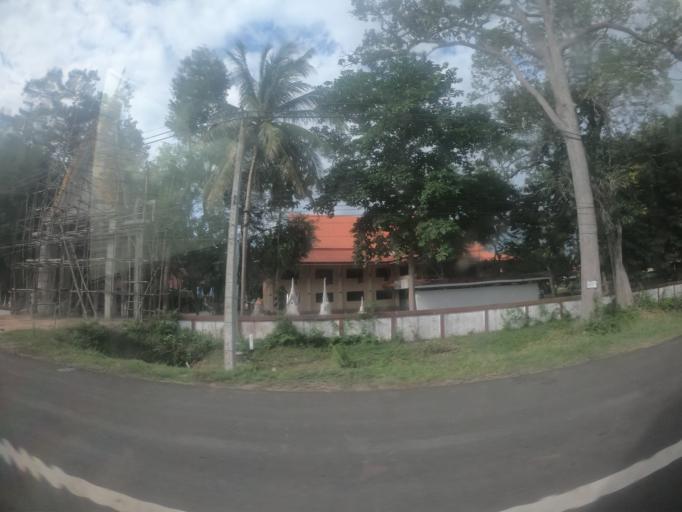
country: TH
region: Surin
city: Prasat
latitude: 14.5878
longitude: 103.4695
